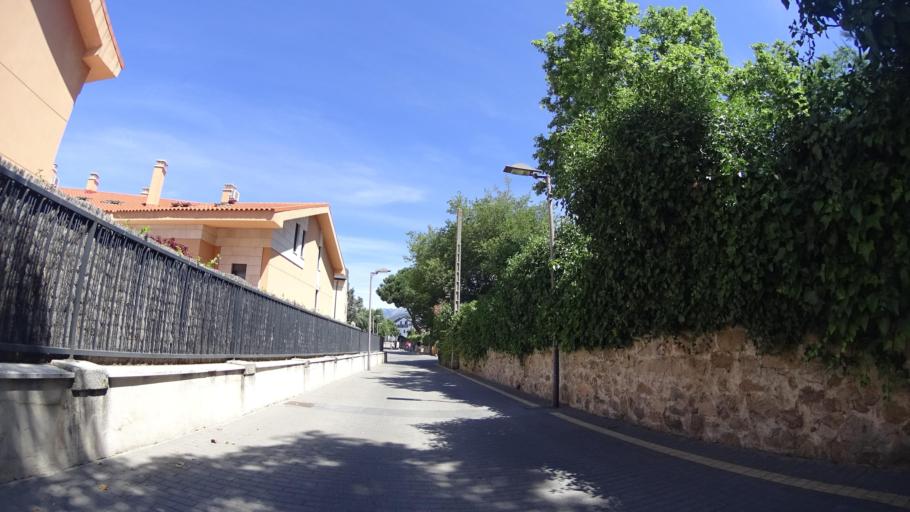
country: ES
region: Madrid
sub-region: Provincia de Madrid
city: Collado-Villalba
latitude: 40.6437
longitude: -3.9925
